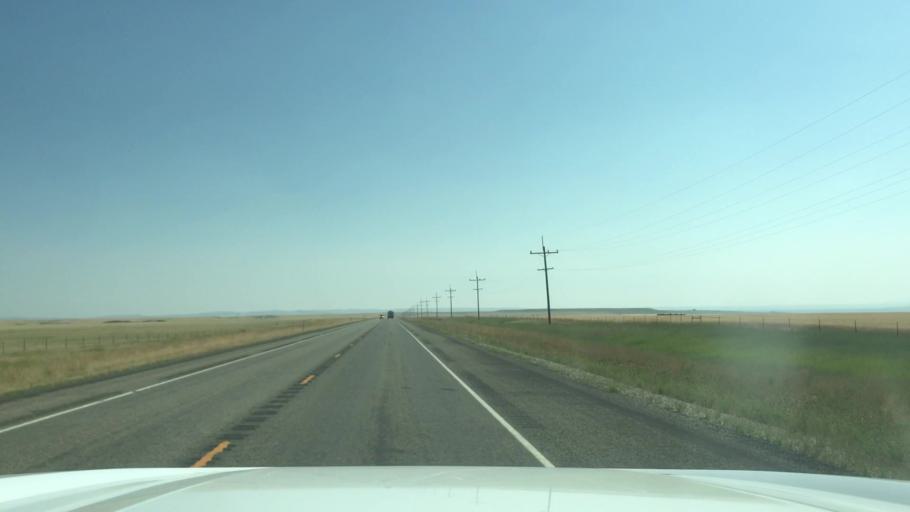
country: US
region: Montana
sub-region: Wheatland County
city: Harlowton
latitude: 46.5076
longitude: -109.7662
